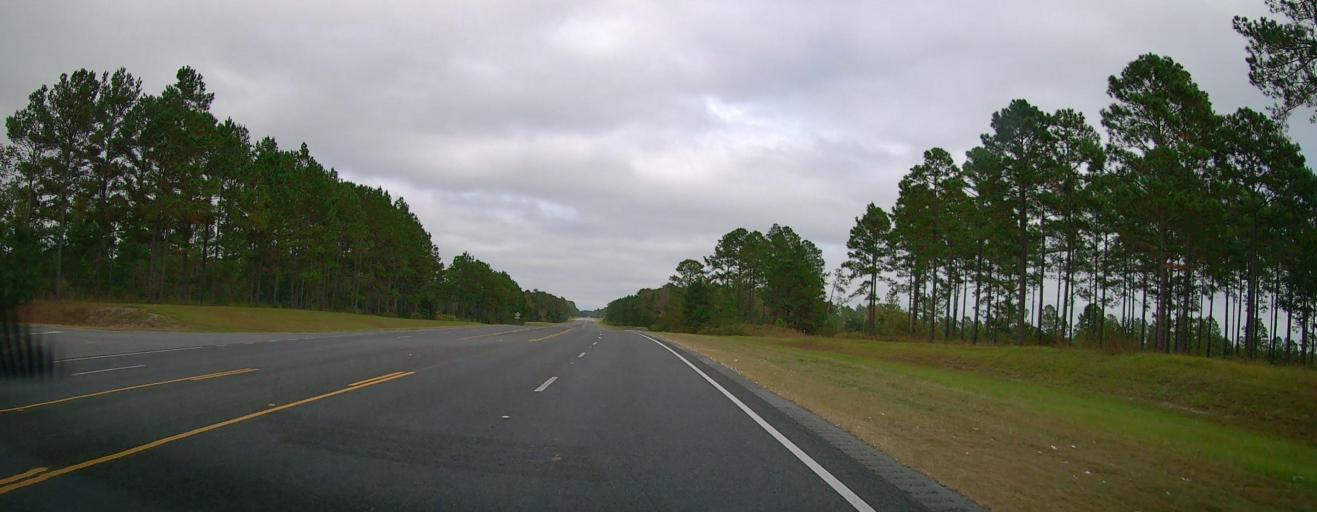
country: US
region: Georgia
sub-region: Colquitt County
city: Moultrie
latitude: 31.0455
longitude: -83.8422
